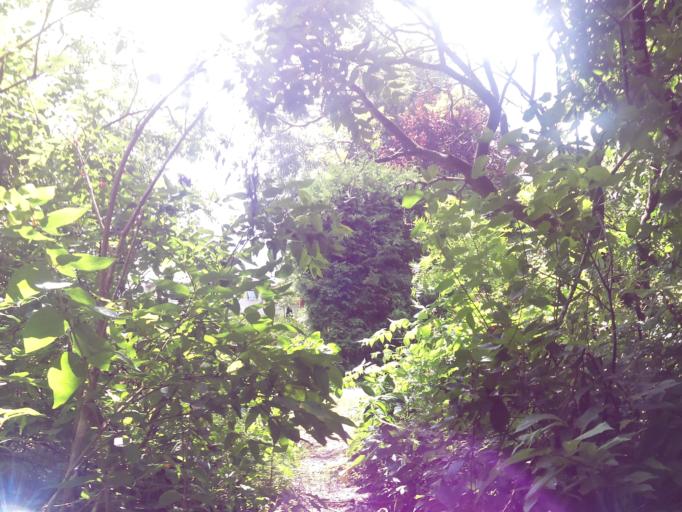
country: CA
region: Ontario
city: Bells Corners
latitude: 45.3254
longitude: -75.9186
